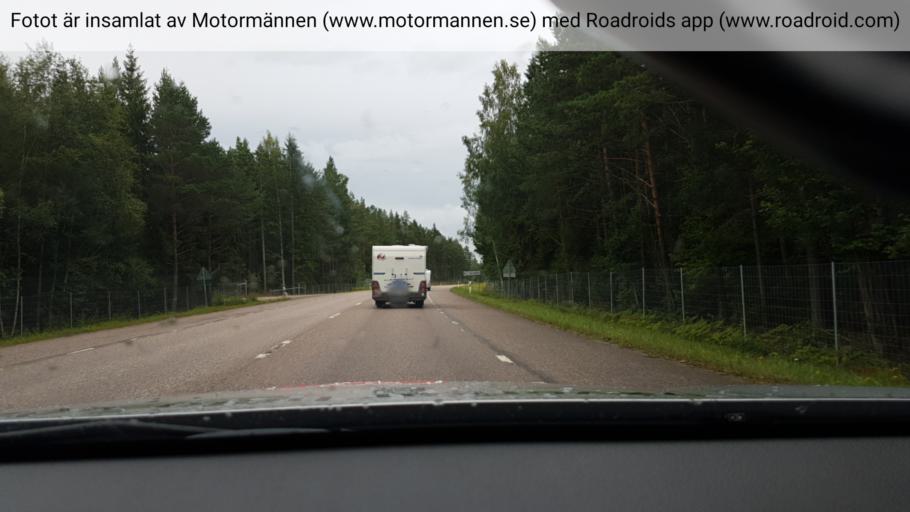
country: SE
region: Uppsala
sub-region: Alvkarleby Kommun
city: AElvkarleby
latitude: 60.5982
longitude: 17.4603
